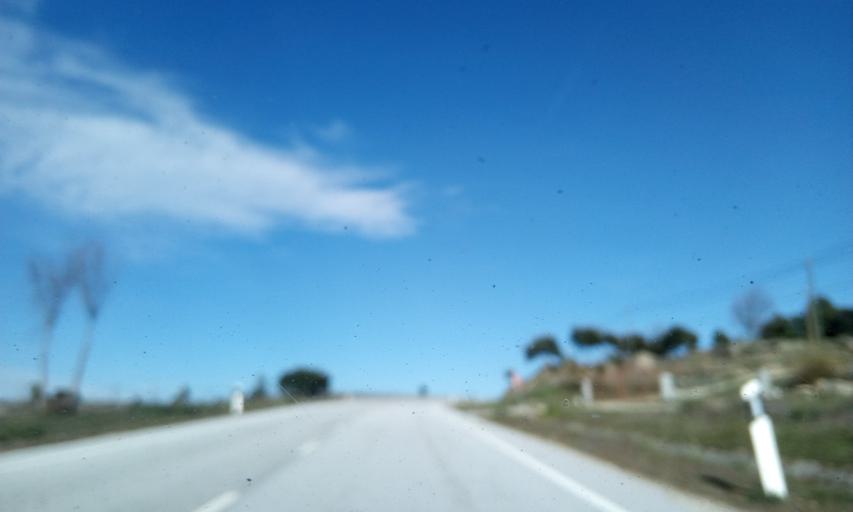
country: ES
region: Castille and Leon
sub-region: Provincia de Salamanca
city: Fuentes de Onoro
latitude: 40.6130
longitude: -6.8859
